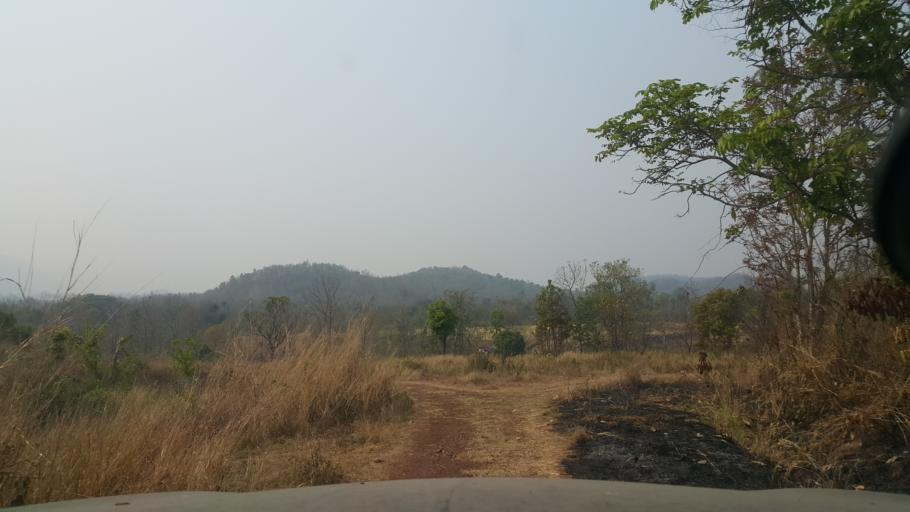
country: TH
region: Chiang Mai
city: Mae On
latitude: 18.7636
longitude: 99.2719
